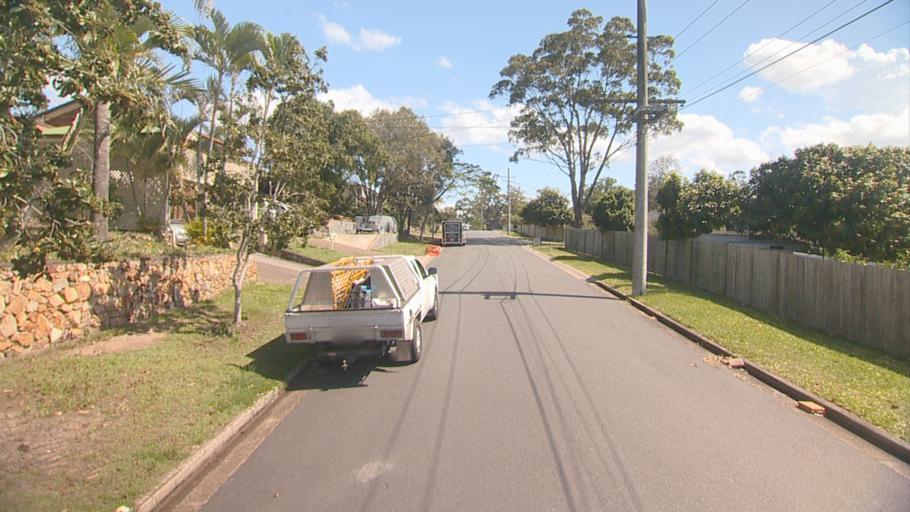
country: AU
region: Queensland
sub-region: Logan
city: Springwood
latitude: -27.6002
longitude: 153.1363
